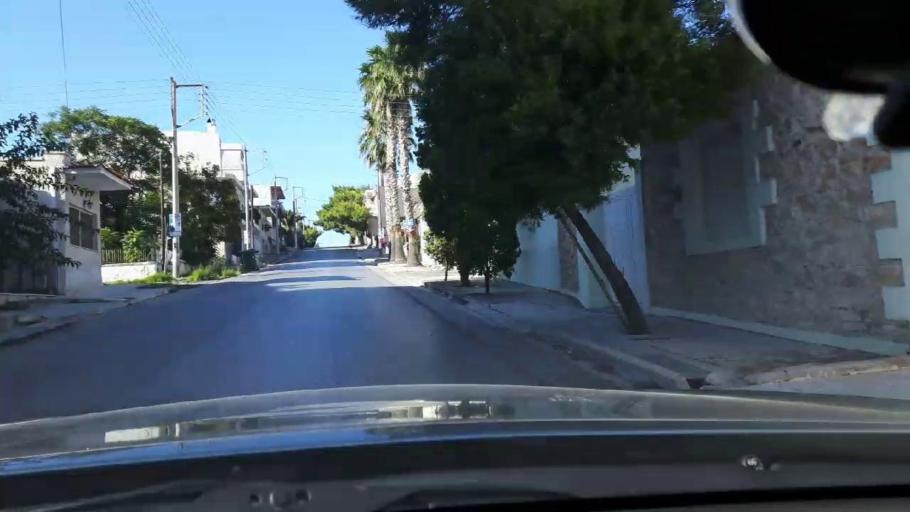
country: GR
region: Attica
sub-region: Nomarchia Anatolikis Attikis
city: Markopoulo
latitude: 37.8810
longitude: 23.9354
